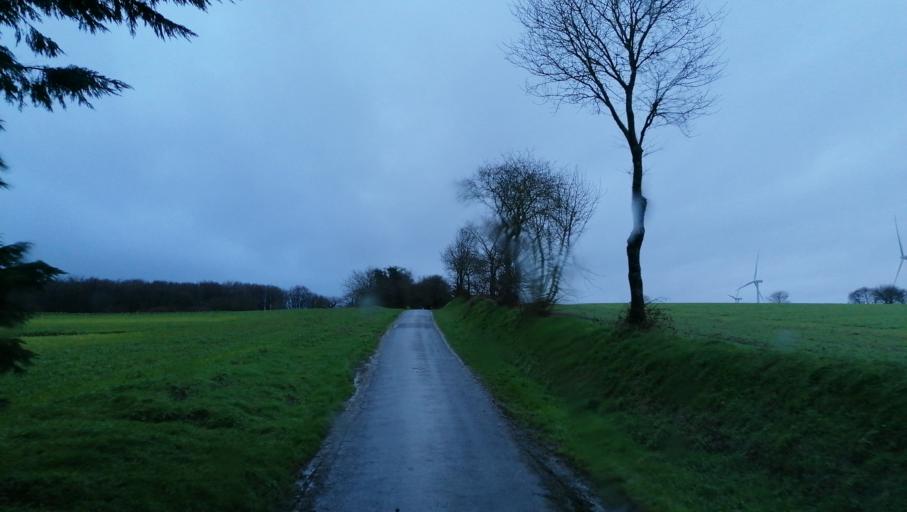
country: FR
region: Brittany
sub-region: Departement des Cotes-d'Armor
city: Lanrodec
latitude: 48.4814
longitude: -2.9988
